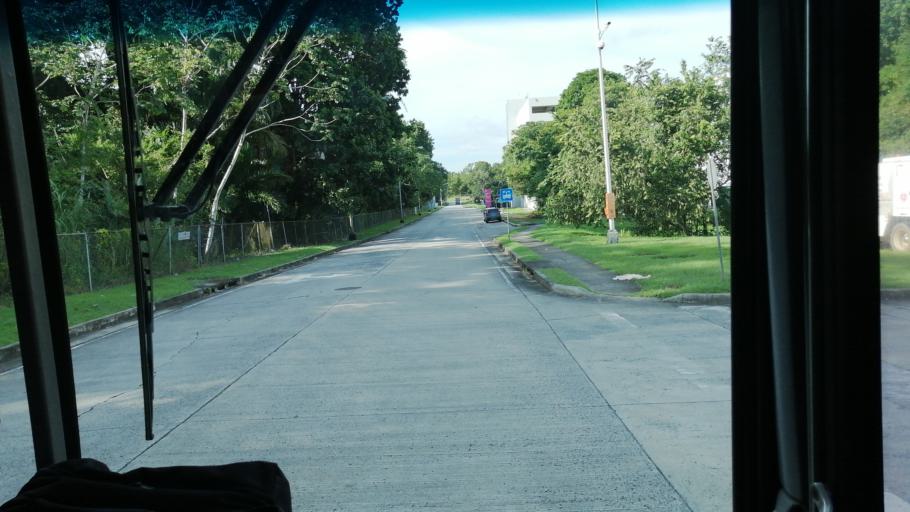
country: PA
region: Panama
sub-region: Distrito de Panama
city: Ancon
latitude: 8.9244
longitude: -79.5944
